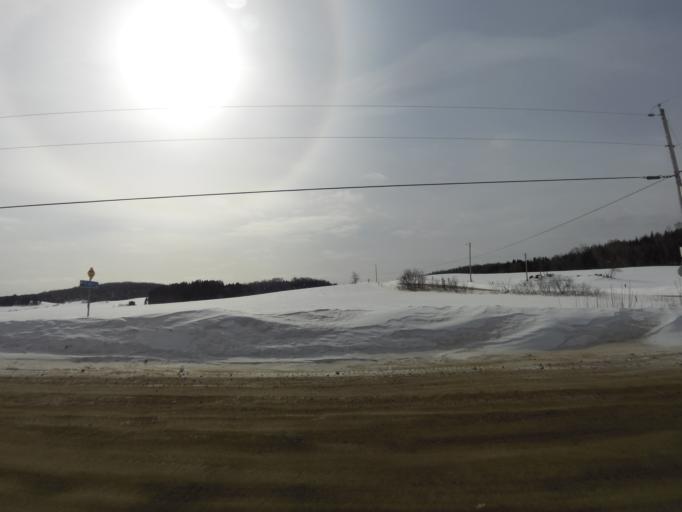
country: CA
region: Quebec
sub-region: Laurentides
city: Ferme-Neuve
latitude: 46.8969
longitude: -75.3335
